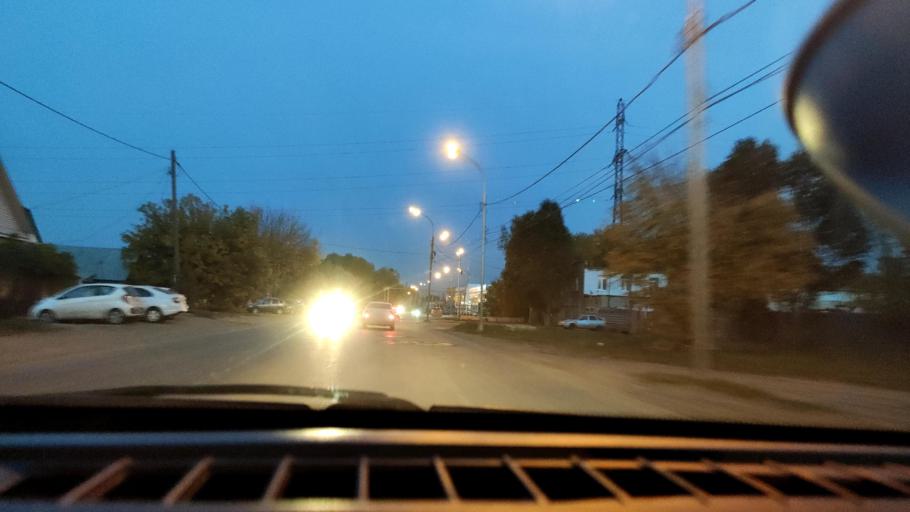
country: RU
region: Samara
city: Samara
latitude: 53.1349
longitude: 50.1141
